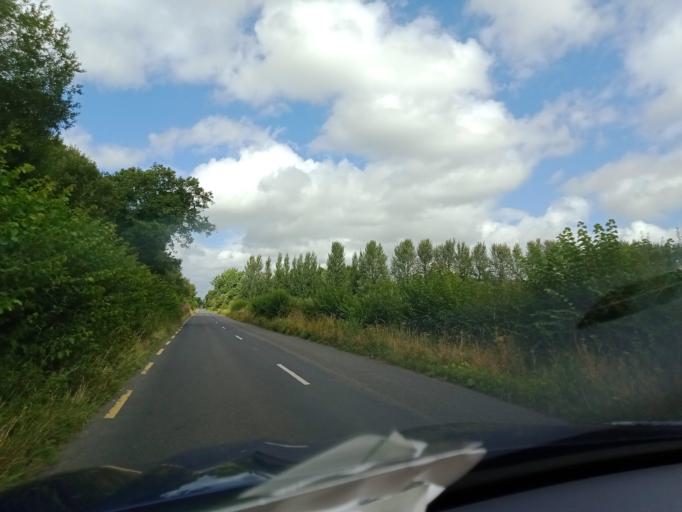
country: IE
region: Leinster
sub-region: Laois
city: Portlaoise
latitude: 52.9834
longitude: -7.2876
